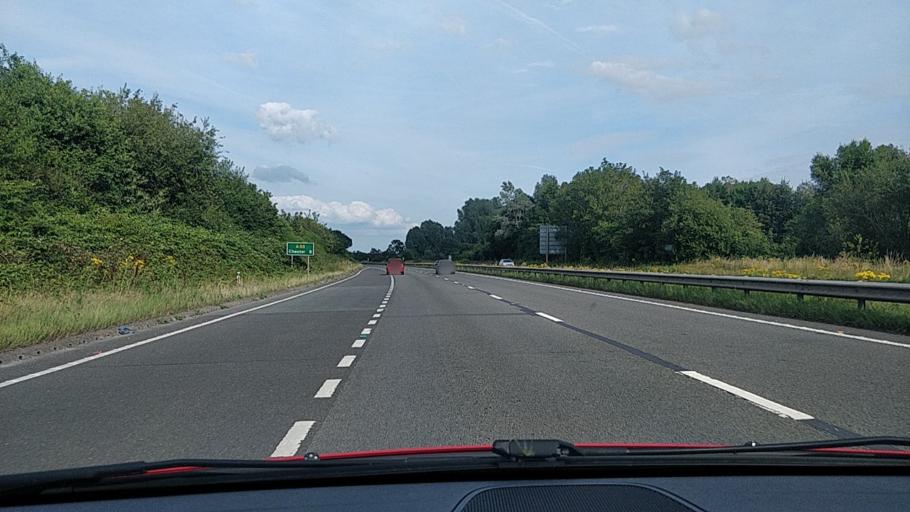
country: GB
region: Wales
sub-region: County of Flintshire
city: Hawarden
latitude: 53.1606
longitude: -3.0022
